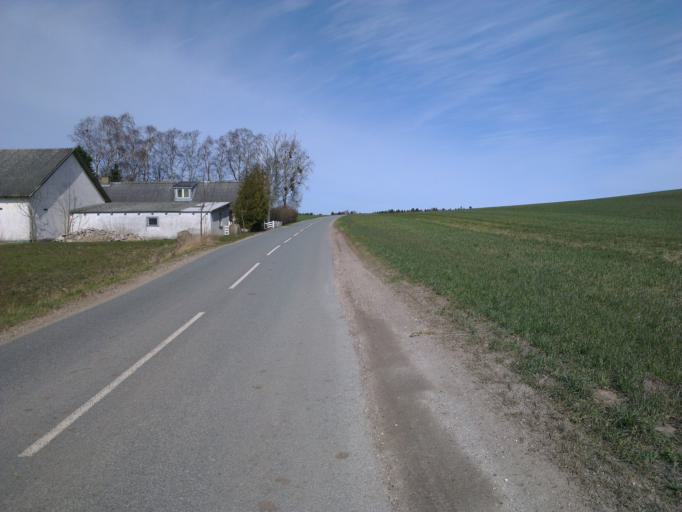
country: DK
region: Capital Region
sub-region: Egedal Kommune
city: Olstykke
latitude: 55.8433
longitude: 12.1254
